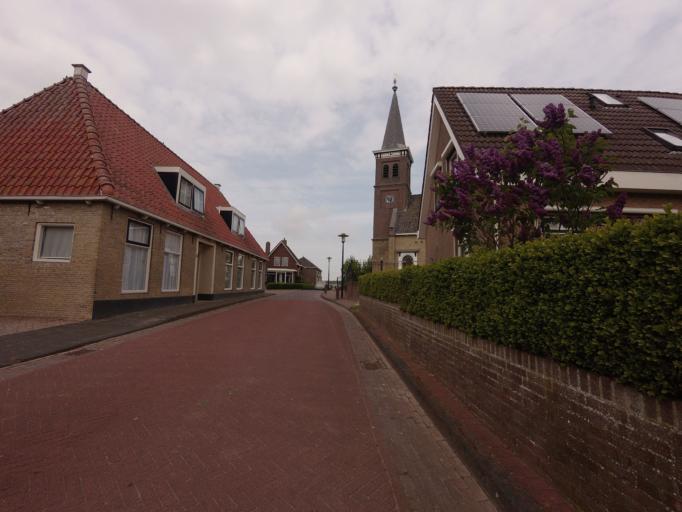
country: NL
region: Friesland
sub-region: Sudwest Fryslan
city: Bolsward
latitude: 53.0831
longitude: 5.4835
